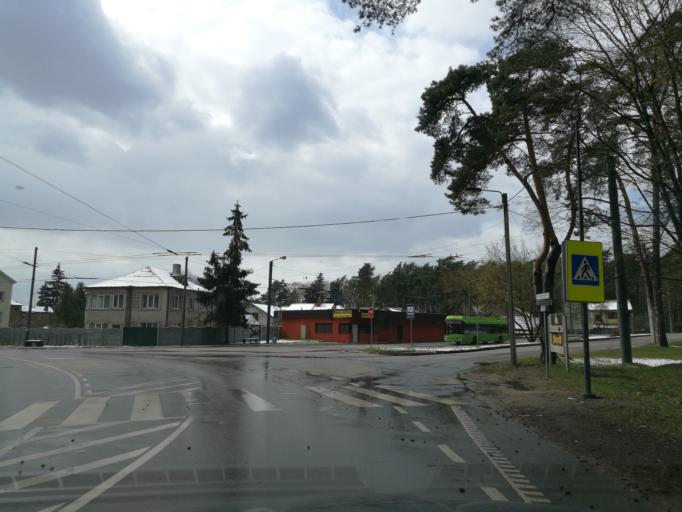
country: LT
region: Kauno apskritis
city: Dainava (Kaunas)
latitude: 54.8716
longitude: 23.9783
